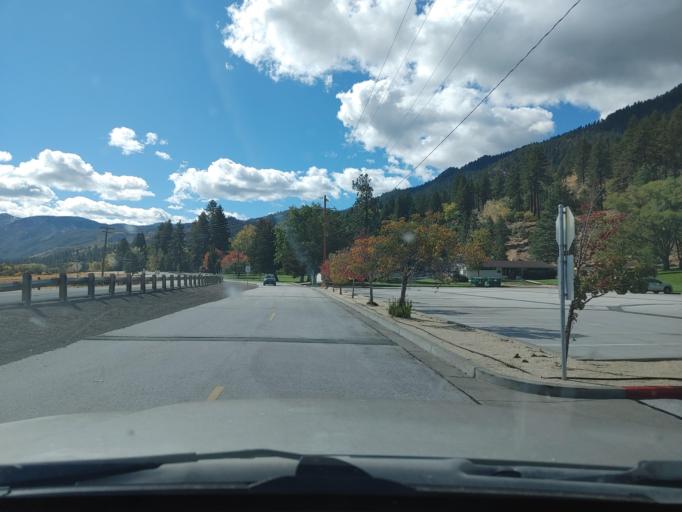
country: US
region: Nevada
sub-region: Washoe County
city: Incline Village
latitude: 39.2865
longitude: -119.8392
